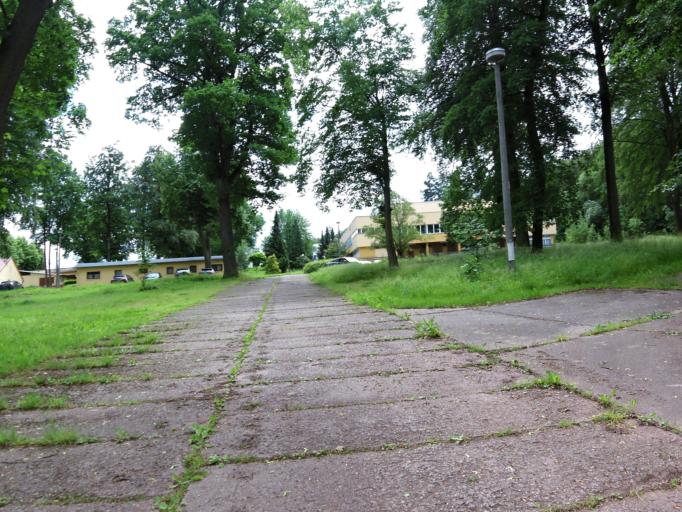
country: DE
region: Thuringia
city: Wolfsburg-Unkeroda
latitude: 50.9191
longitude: 10.2996
